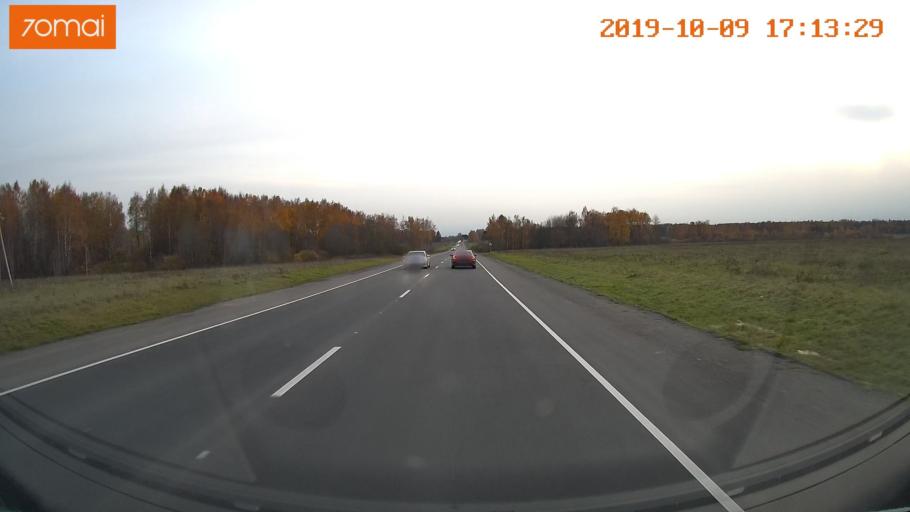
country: RU
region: Ivanovo
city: Privolzhsk
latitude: 57.3145
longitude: 41.2233
